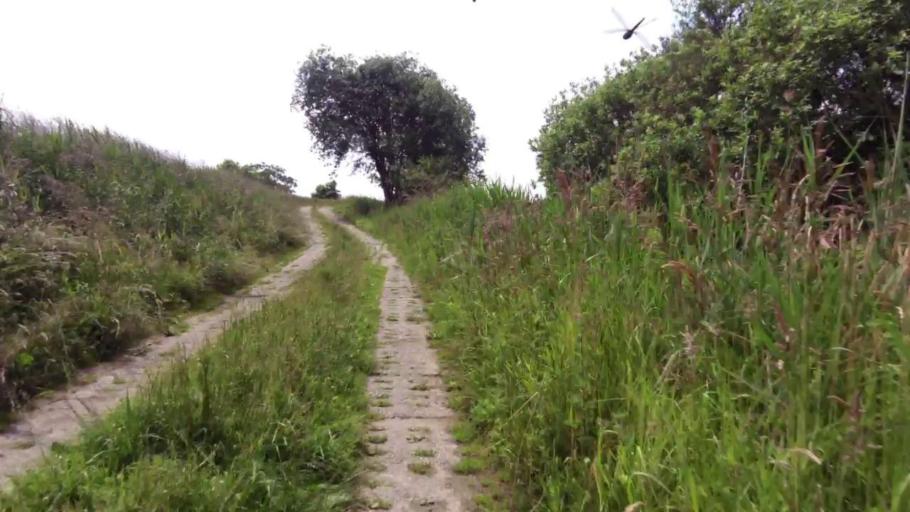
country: PL
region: West Pomeranian Voivodeship
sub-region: Powiat goleniowski
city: Stepnica
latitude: 53.7320
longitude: 14.6205
